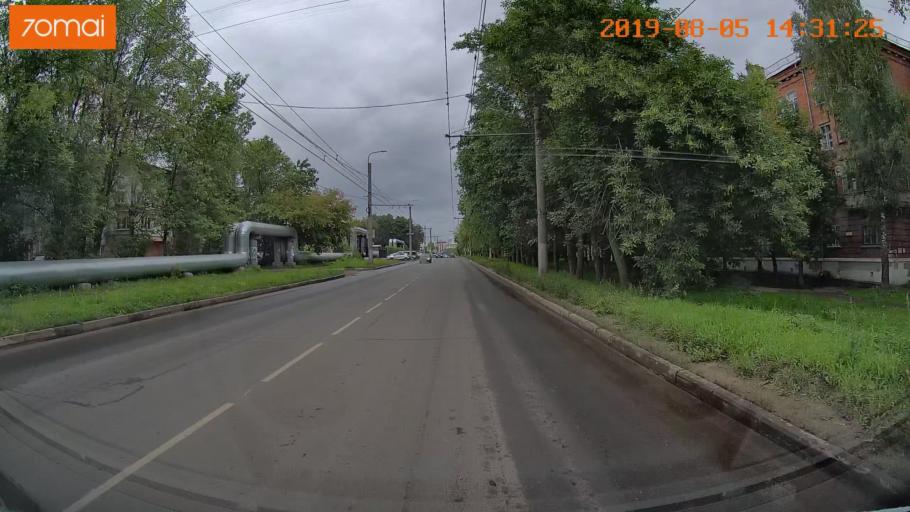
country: RU
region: Ivanovo
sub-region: Gorod Ivanovo
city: Ivanovo
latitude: 56.9866
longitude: 41.0026
